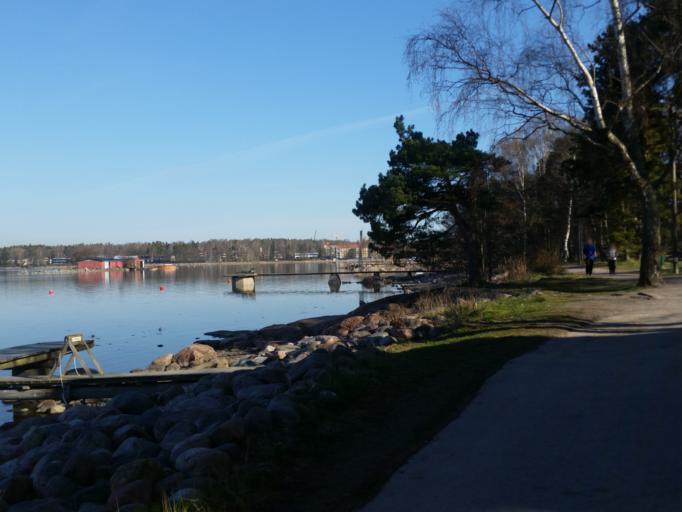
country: FI
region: Uusimaa
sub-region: Helsinki
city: Teekkarikylae
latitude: 60.1480
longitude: 24.8764
